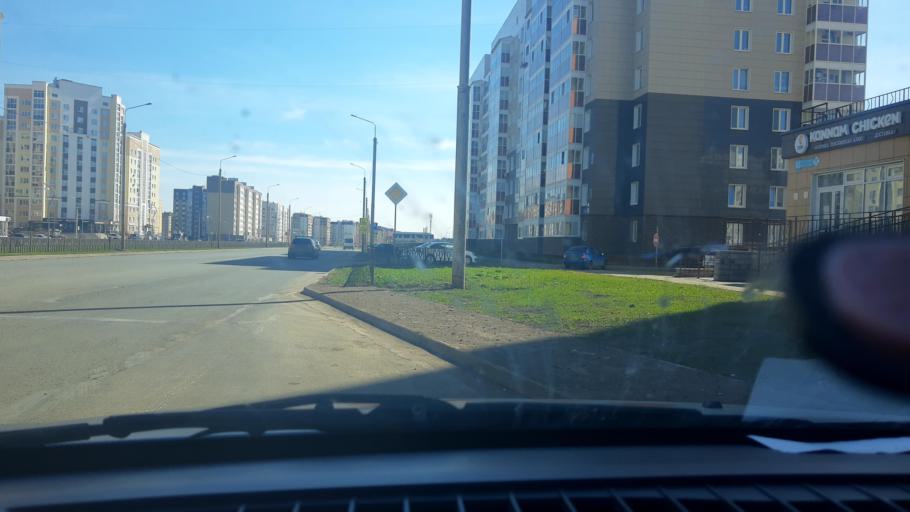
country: RU
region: Bashkortostan
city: Sterlitamak
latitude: 53.6280
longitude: 55.8957
